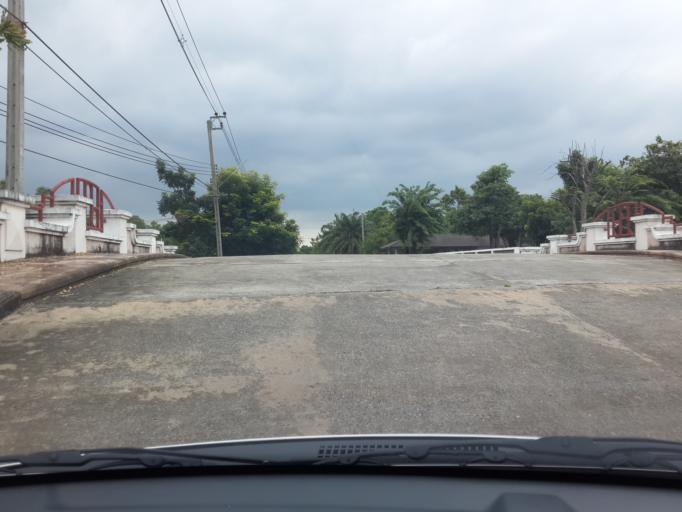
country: TH
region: Bangkok
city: Khlong Sam Wa
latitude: 13.8398
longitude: 100.7553
